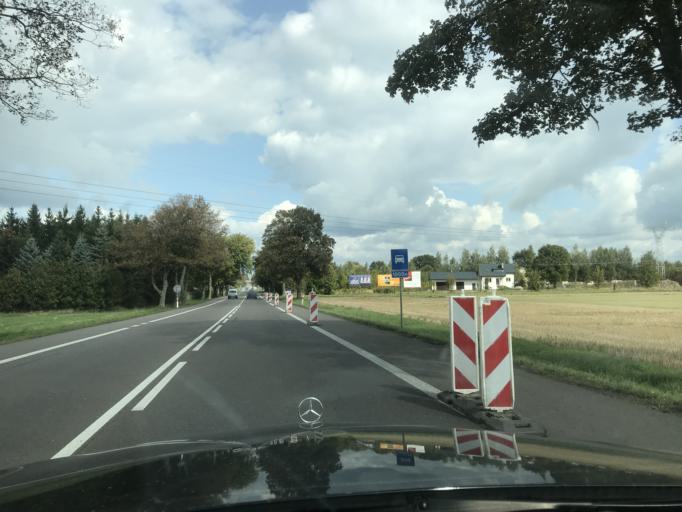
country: PL
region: Lublin Voivodeship
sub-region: Powiat lubelski
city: Kozubszczyzna
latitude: 51.1921
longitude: 22.4368
